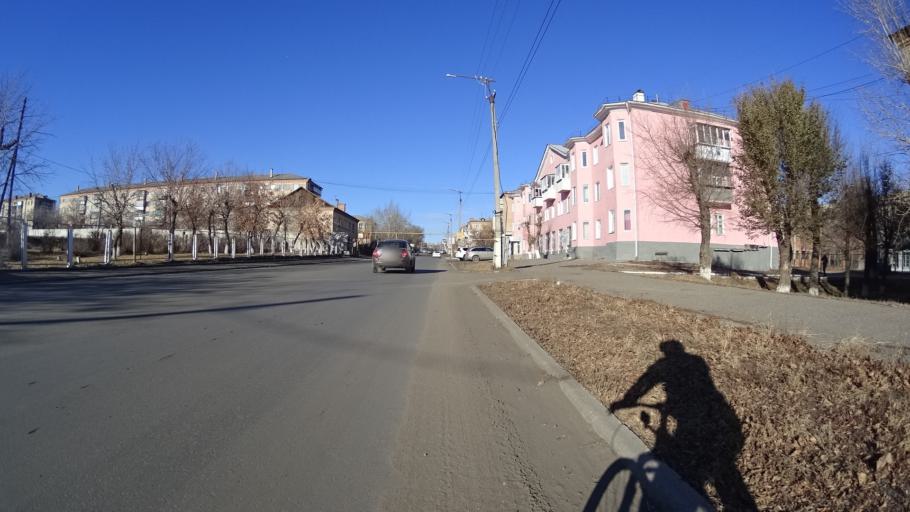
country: RU
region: Chelyabinsk
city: Troitsk
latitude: 54.0780
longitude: 61.5384
